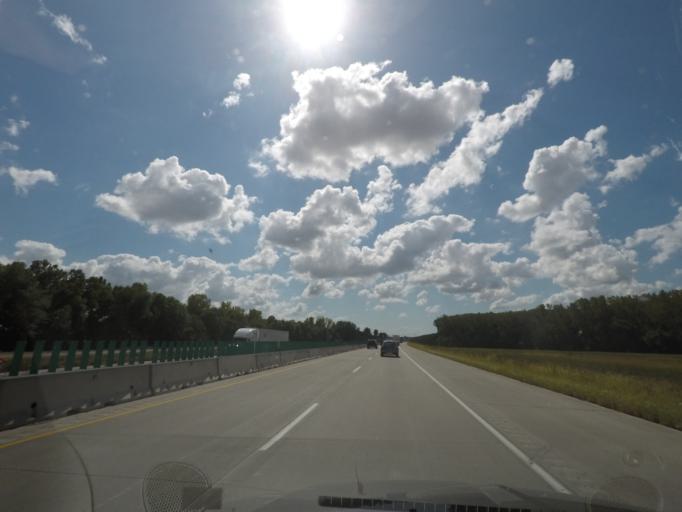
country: US
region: Iowa
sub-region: Story County
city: Huxley
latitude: 41.9595
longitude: -93.5702
